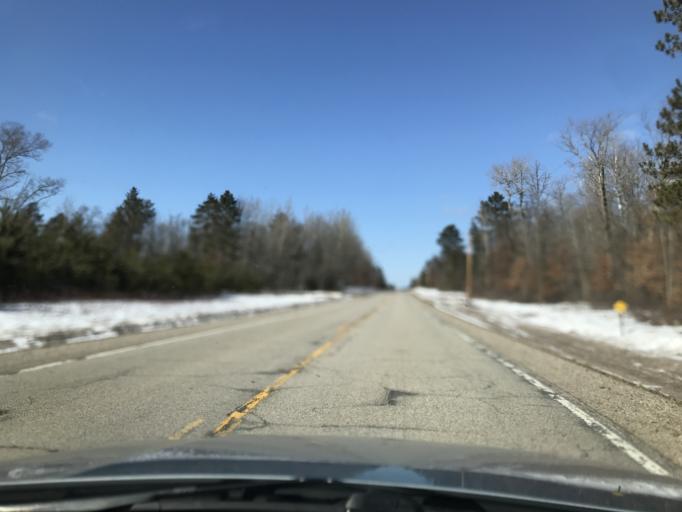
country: US
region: Wisconsin
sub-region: Marinette County
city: Niagara
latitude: 45.3539
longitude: -88.1010
